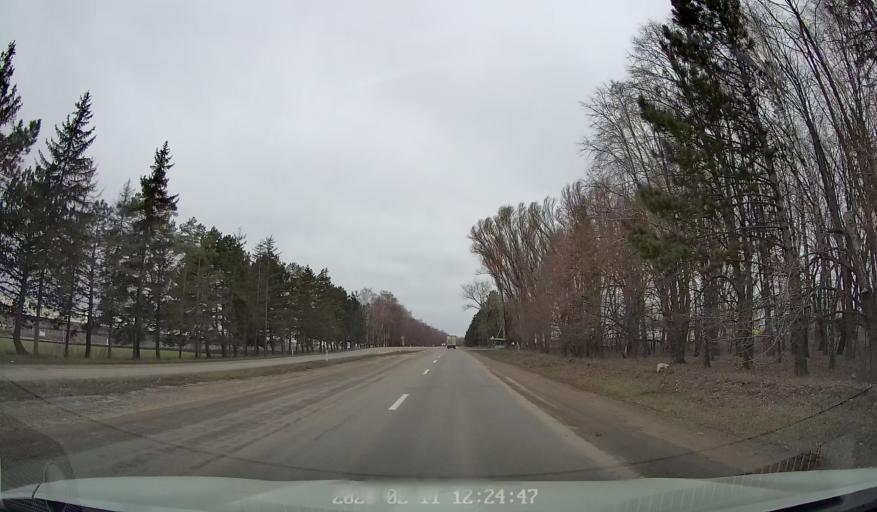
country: MD
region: Raionul Edinet
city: Edinet
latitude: 48.1500
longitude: 27.3428
